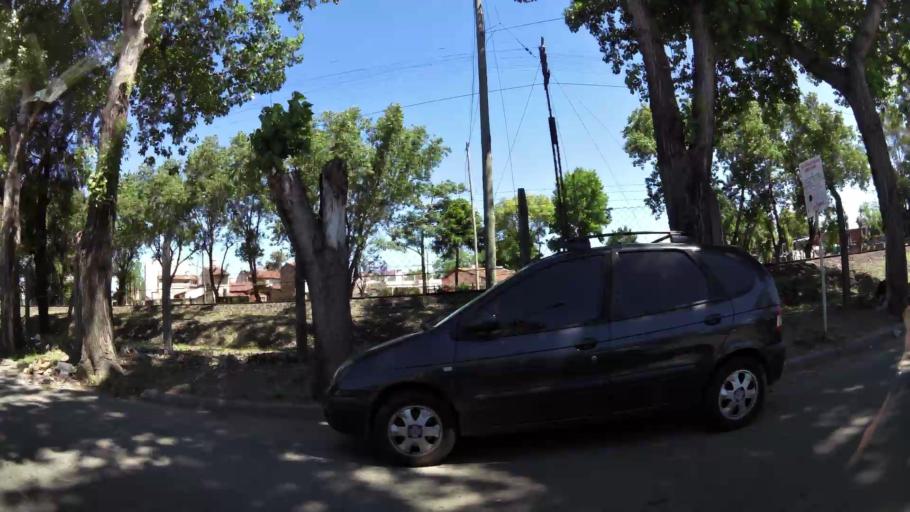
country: AR
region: Buenos Aires
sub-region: Partido de San Isidro
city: San Isidro
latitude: -34.5066
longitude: -58.5800
